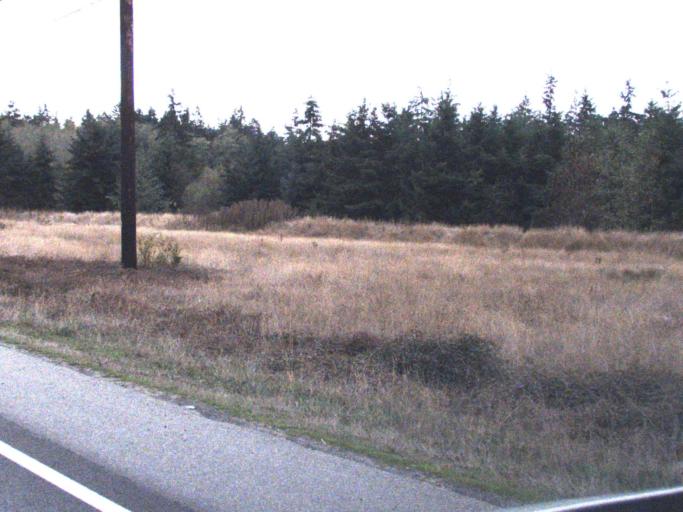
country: US
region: Washington
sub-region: Island County
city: Camano
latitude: 48.1256
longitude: -122.5888
